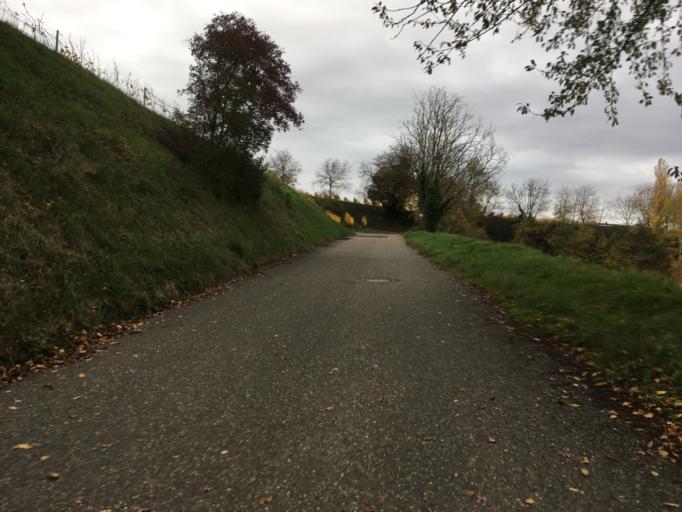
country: DE
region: Baden-Wuerttemberg
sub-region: Freiburg Region
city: Merdingen
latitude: 48.0172
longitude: 7.6985
